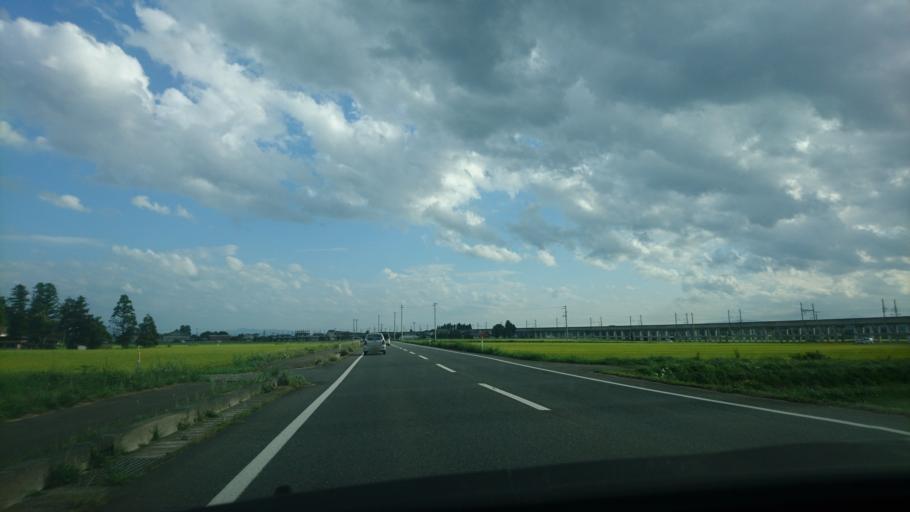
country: JP
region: Iwate
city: Kitakami
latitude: 39.2438
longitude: 141.1180
